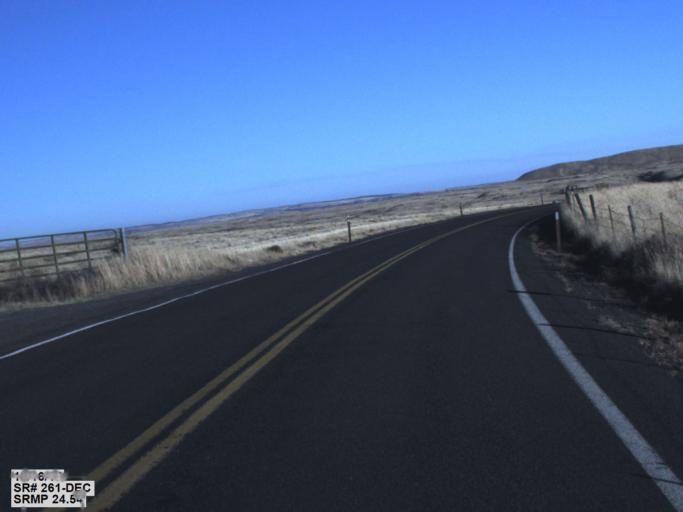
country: US
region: Washington
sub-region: Walla Walla County
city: Waitsburg
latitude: 46.6776
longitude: -118.3342
